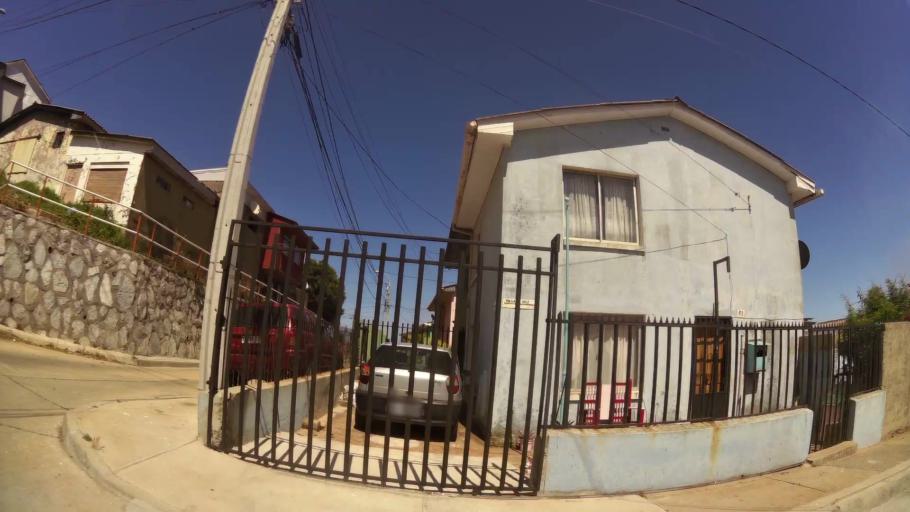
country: CL
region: Valparaiso
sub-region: Provincia de Valparaiso
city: Valparaiso
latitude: -33.0402
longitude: -71.6526
